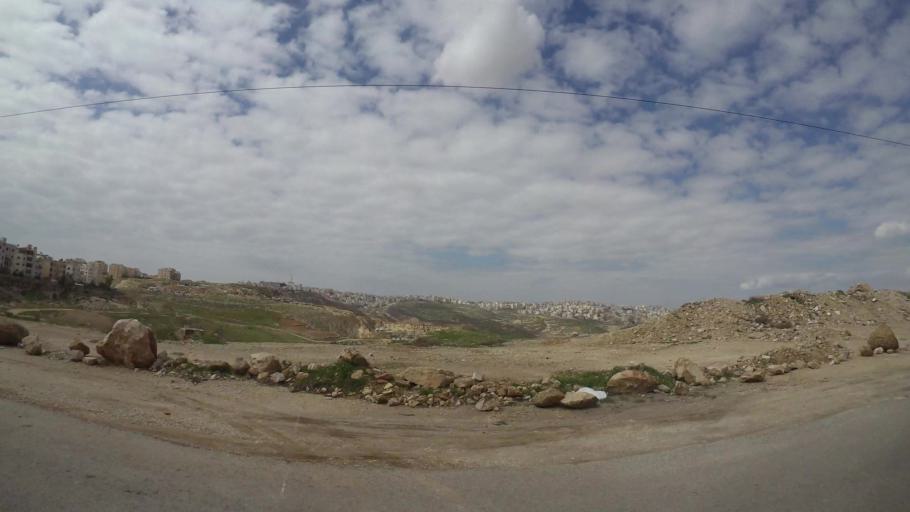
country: JO
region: Amman
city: Amman
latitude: 32.0004
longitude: 35.9148
